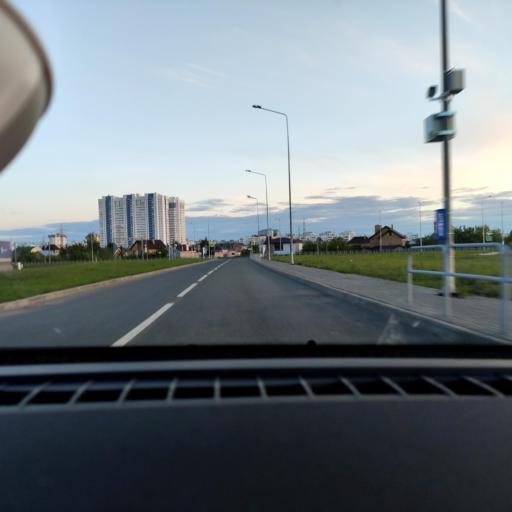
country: RU
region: Samara
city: Samara
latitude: 53.2722
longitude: 50.2353
